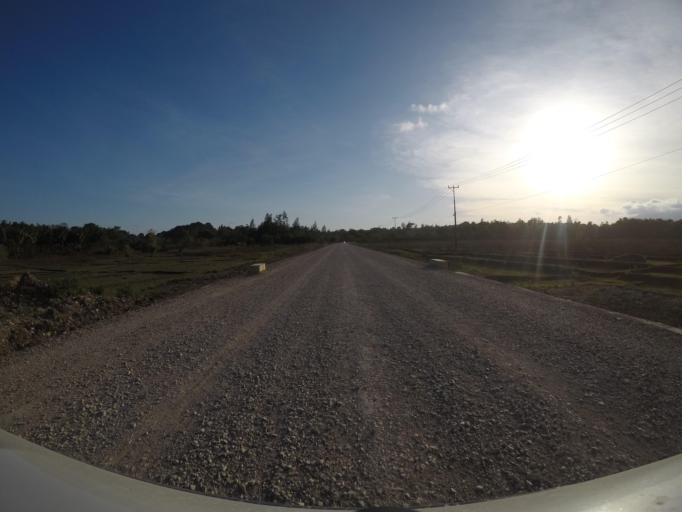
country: TL
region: Viqueque
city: Viqueque
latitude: -8.8294
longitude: 126.5248
